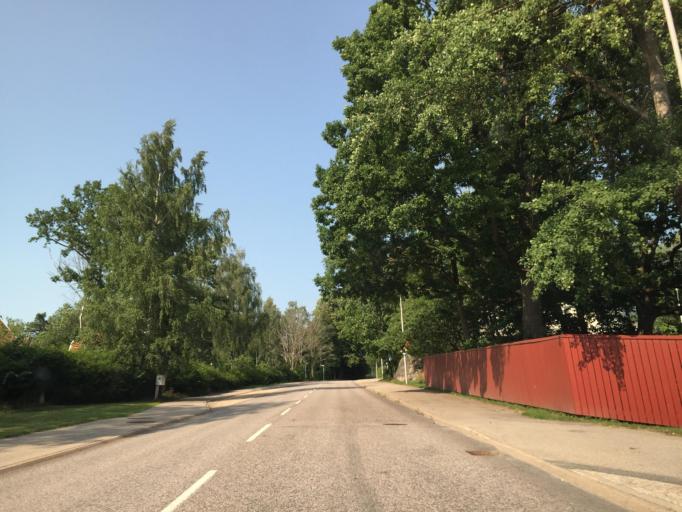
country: SE
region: Vaestra Goetaland
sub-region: Vanersborgs Kommun
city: Vanersborg
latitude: 58.3724
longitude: 12.2867
